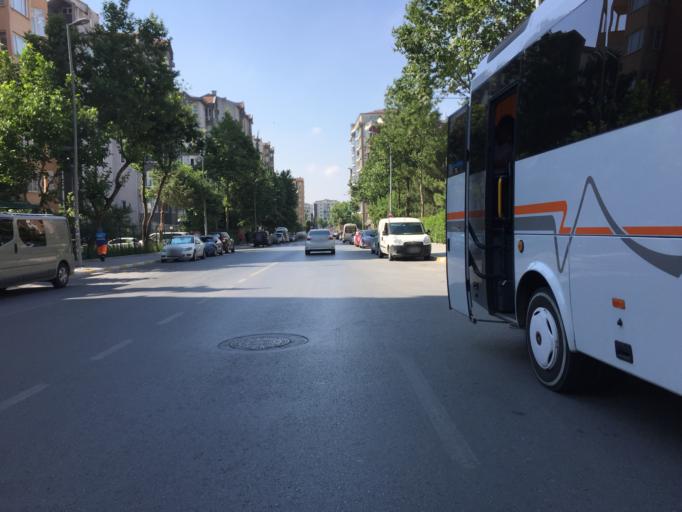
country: TR
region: Istanbul
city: Esenyurt
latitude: 41.0610
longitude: 28.6721
